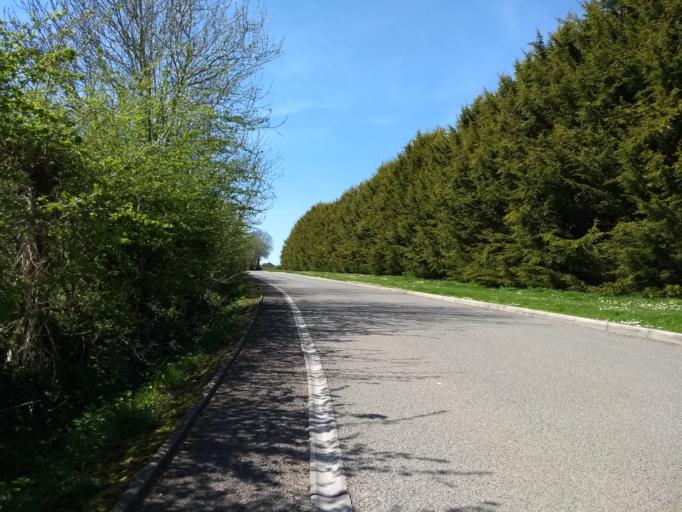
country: GB
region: England
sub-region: Isle of Wight
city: Northwood
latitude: 50.7402
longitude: -1.3020
